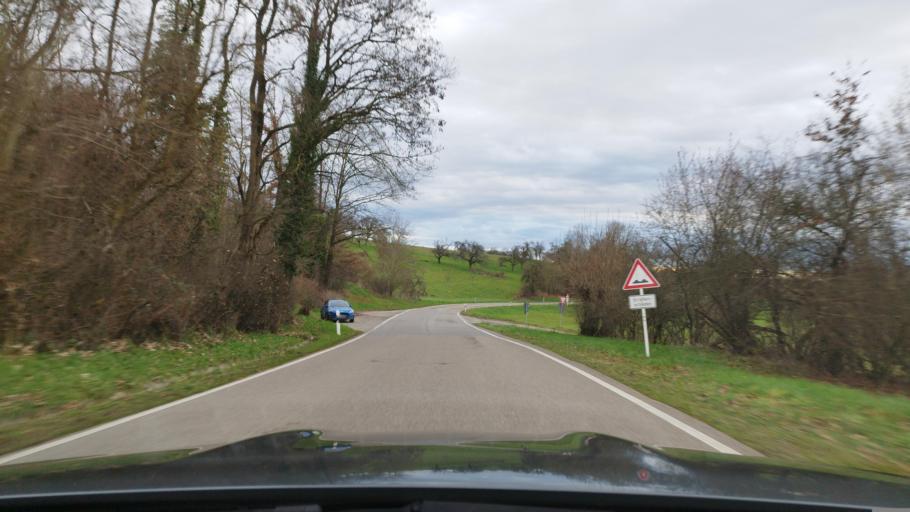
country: DE
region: Baden-Wuerttemberg
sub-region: Regierungsbezirk Stuttgart
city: Burgstetten
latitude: 48.9397
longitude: 9.3588
